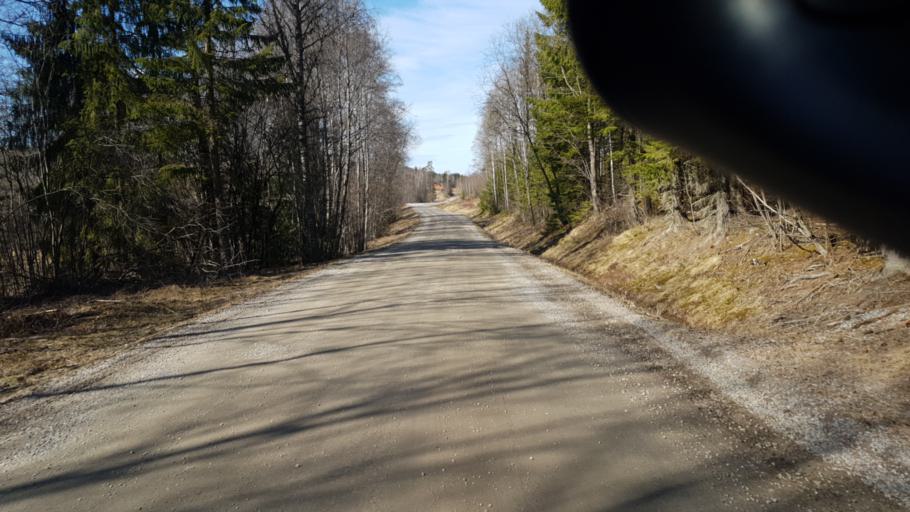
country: SE
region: Vaermland
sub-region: Sunne Kommun
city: Sunne
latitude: 59.6768
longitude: 12.9004
